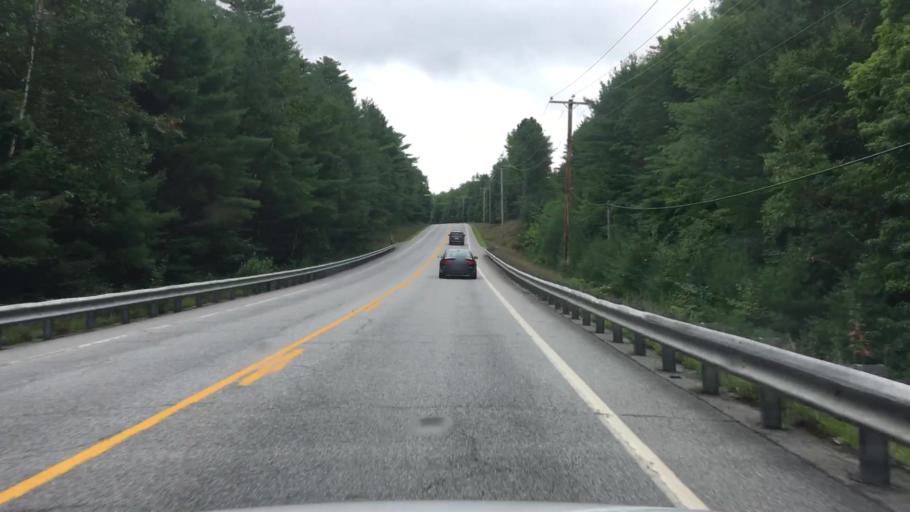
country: US
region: Maine
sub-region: Oxford County
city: Hiram
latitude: 43.8505
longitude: -70.7895
